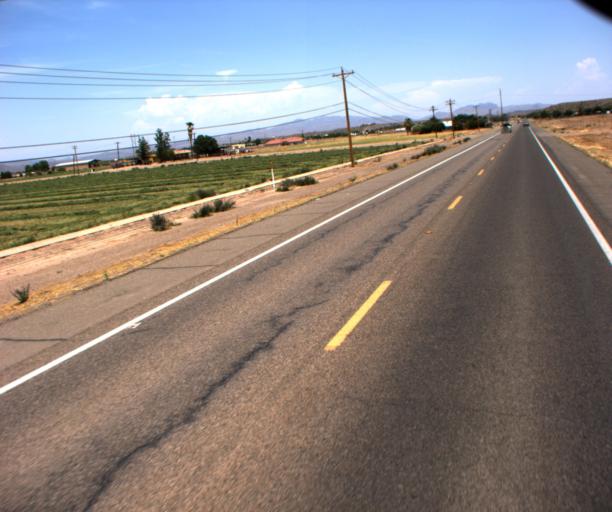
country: US
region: Arizona
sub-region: Graham County
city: Safford
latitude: 32.8128
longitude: -109.6113
